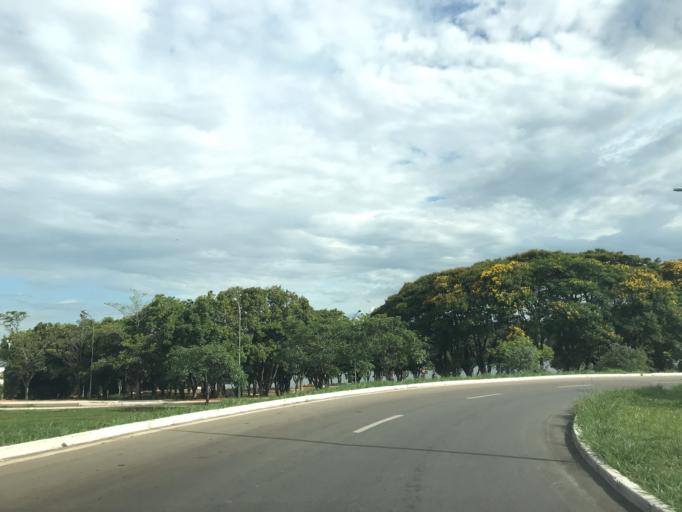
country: BR
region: Federal District
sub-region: Brasilia
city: Brasilia
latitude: -15.8194
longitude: -47.8789
